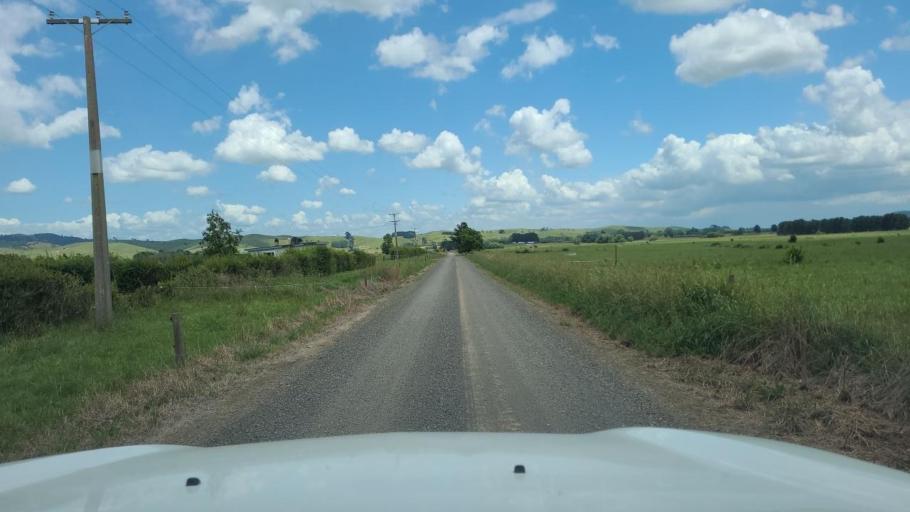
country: NZ
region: Waikato
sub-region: Hauraki District
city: Ngatea
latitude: -37.5224
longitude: 175.4126
